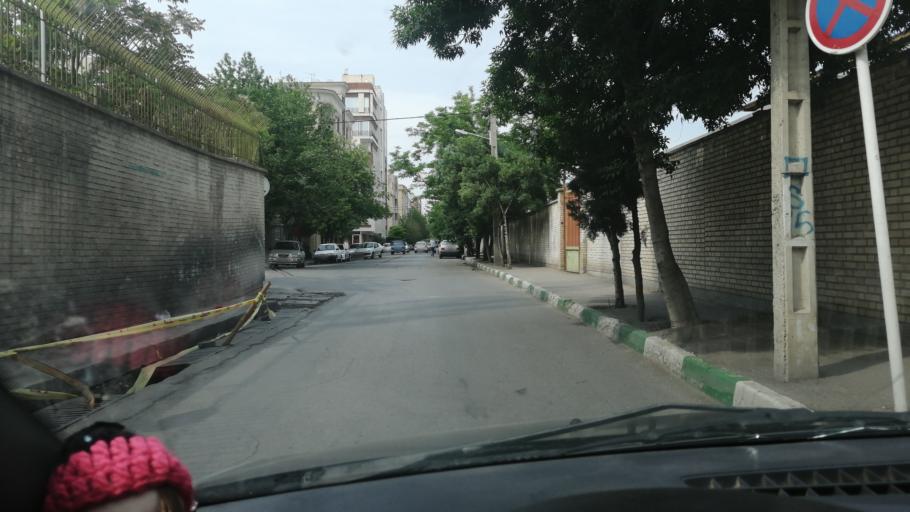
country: IR
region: Razavi Khorasan
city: Mashhad
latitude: 36.3246
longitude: 59.5668
